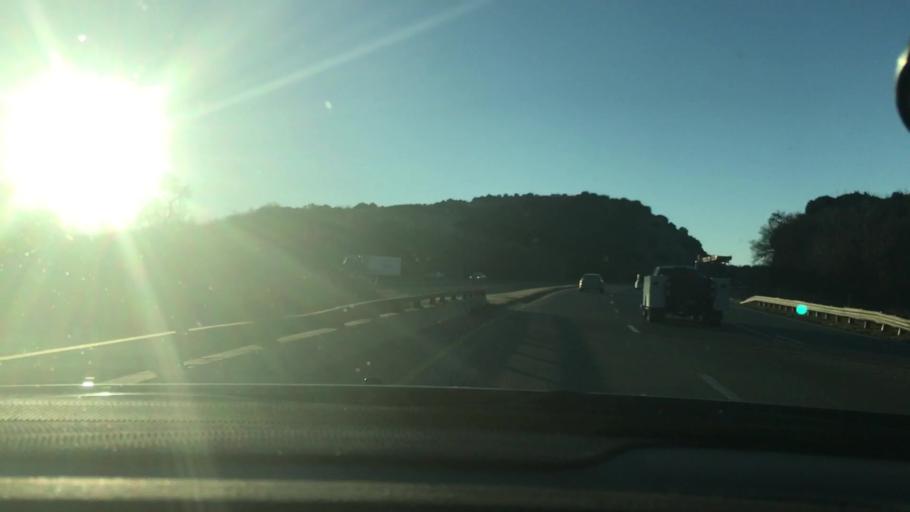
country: US
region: Oklahoma
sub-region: Murray County
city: Davis
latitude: 34.4443
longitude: -97.1299
